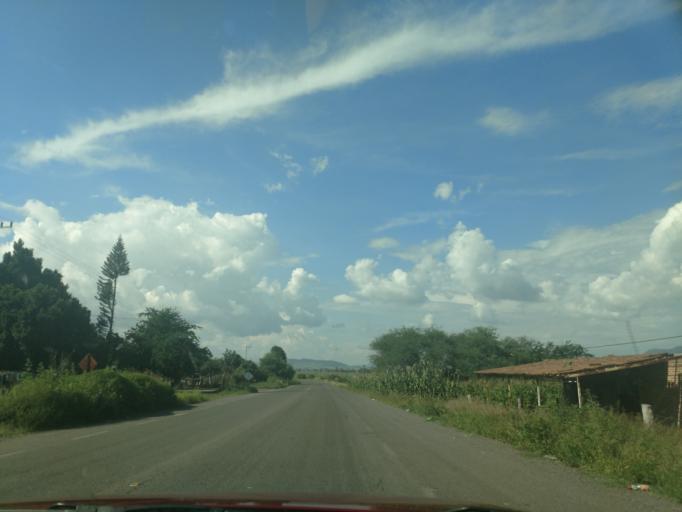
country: MX
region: Jalisco
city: Antonio Escobedo
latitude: 20.8500
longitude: -104.0286
